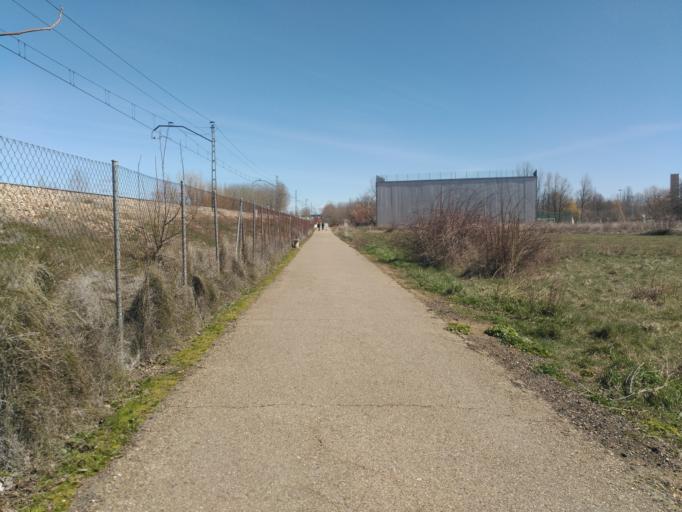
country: ES
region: Castille and Leon
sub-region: Provincia de Leon
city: Villarejo de Orbigo
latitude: 42.4371
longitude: -5.8811
